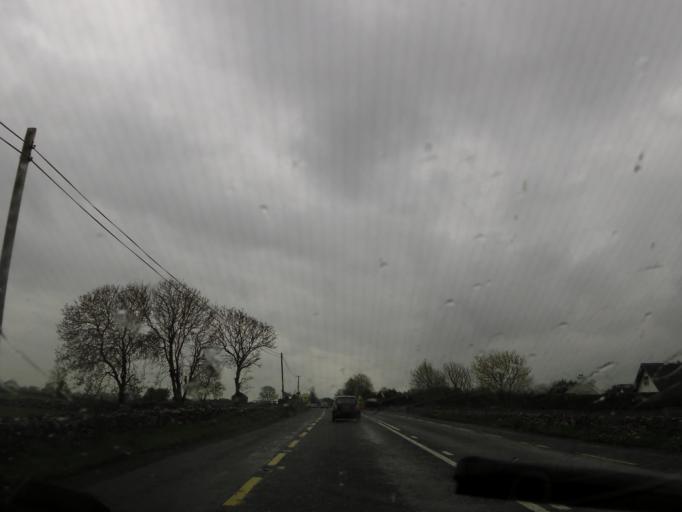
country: IE
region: Connaught
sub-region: County Galway
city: Tuam
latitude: 53.4527
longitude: -8.9094
